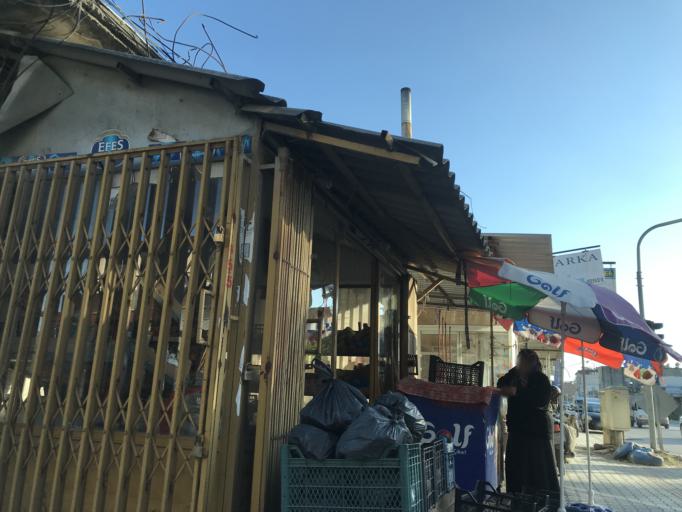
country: TR
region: Hatay
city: Samandag
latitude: 36.0827
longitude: 35.9963
